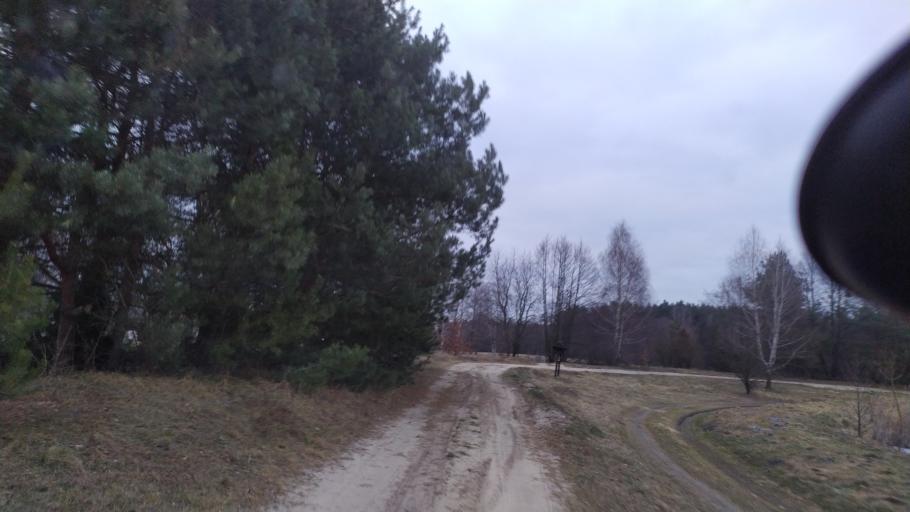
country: PL
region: Lublin Voivodeship
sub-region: Powiat lubartowski
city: Abramow
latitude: 51.4254
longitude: 22.2885
